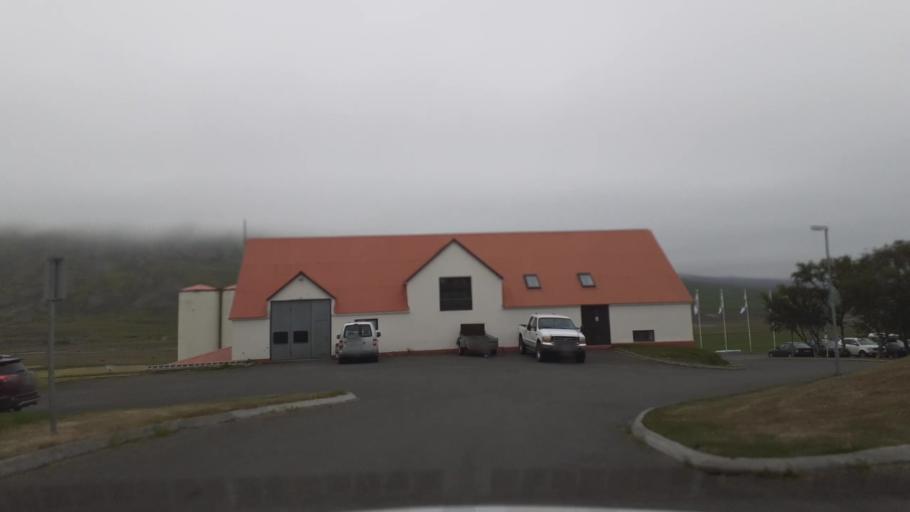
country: IS
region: Northeast
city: Siglufjoerdur
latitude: 65.7329
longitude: -19.1112
